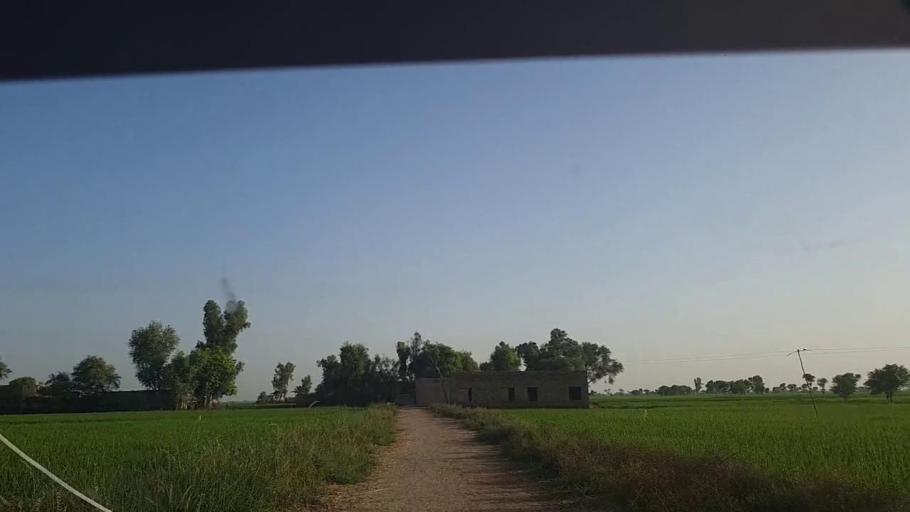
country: PK
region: Sindh
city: Thul
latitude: 28.2114
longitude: 68.8861
